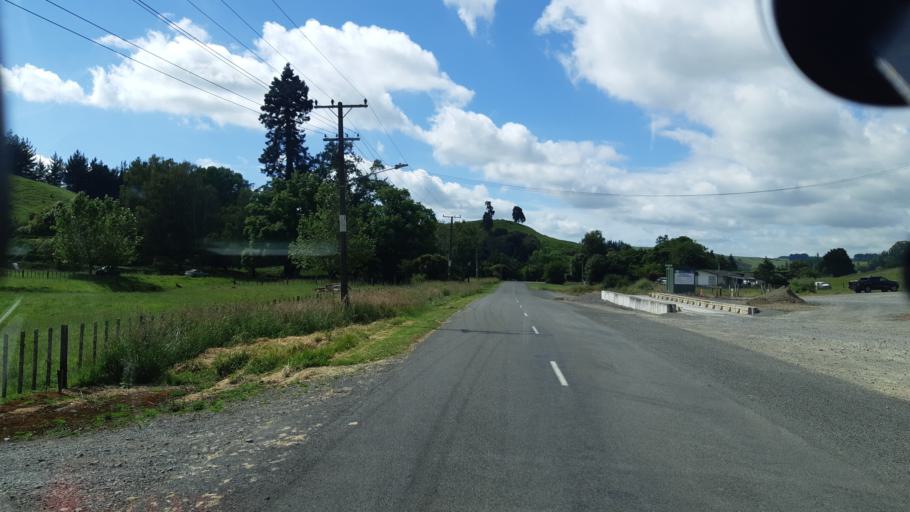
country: NZ
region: Manawatu-Wanganui
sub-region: Rangitikei District
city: Bulls
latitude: -39.9268
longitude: 175.5624
